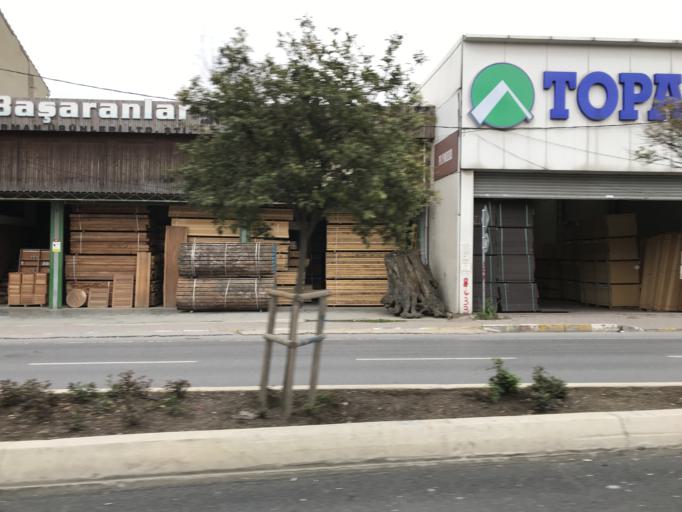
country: TR
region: Istanbul
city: Umraniye
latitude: 41.0076
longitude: 29.1622
